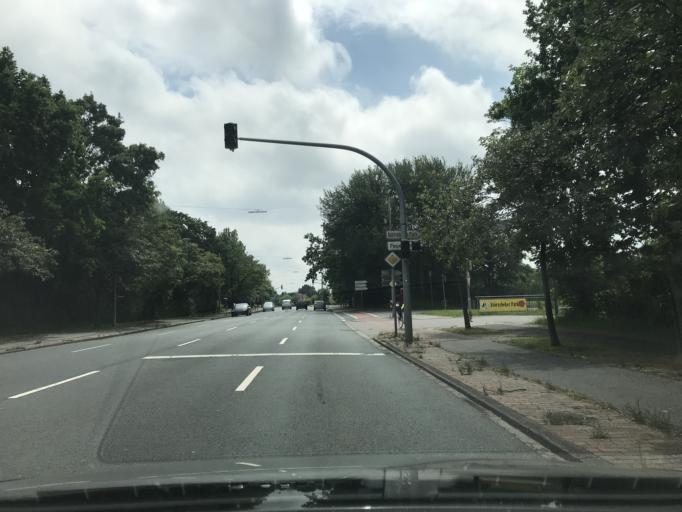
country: DE
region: Lower Saxony
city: Wilhelmshaven
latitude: 53.5623
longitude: 8.1037
